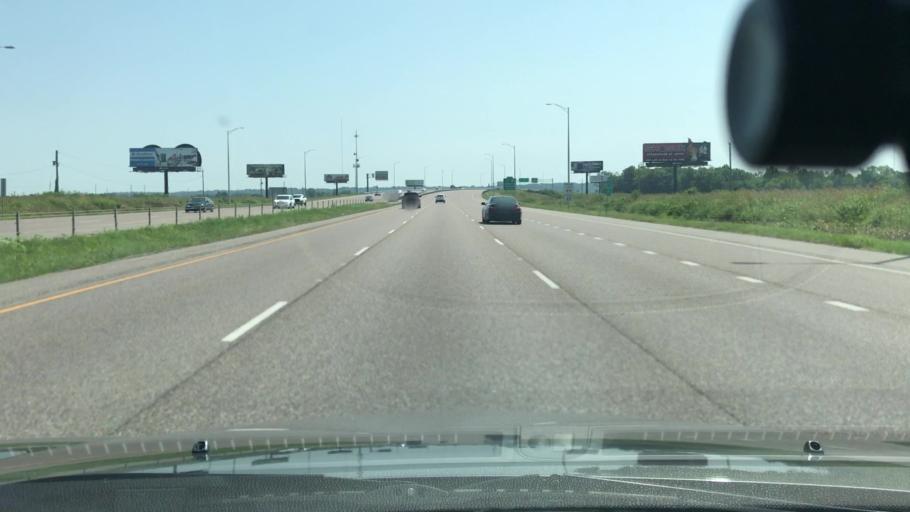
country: US
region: Illinois
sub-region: Saint Clair County
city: Washington Park
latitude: 38.6207
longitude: -90.0883
